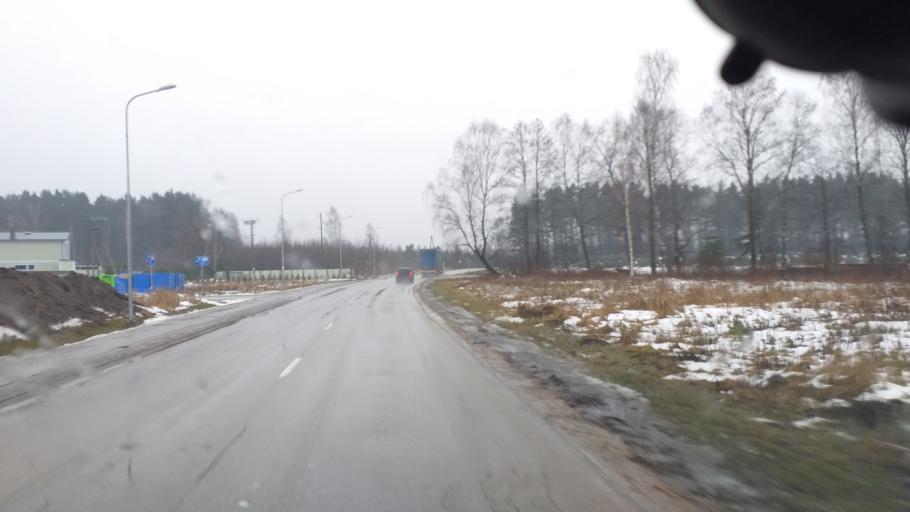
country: LV
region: Babite
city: Pinki
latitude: 56.9734
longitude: 23.9692
